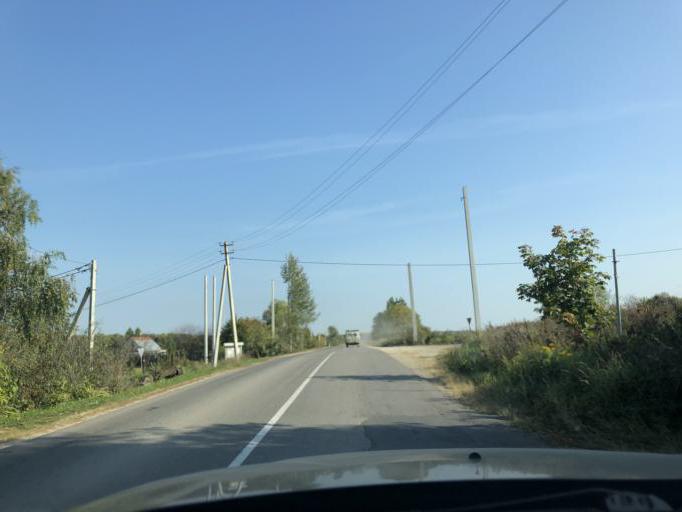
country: RU
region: Tula
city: Novogurovskiy
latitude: 54.4120
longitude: 37.3106
